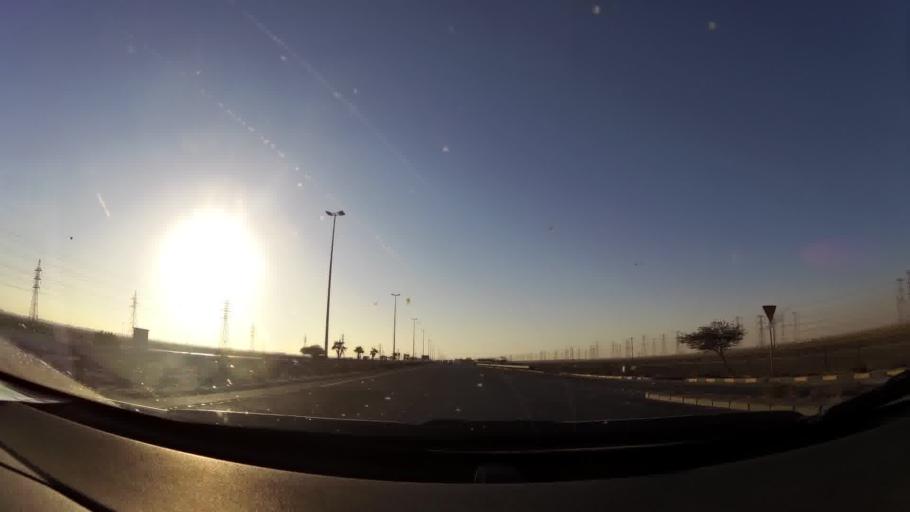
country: KW
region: Al Ahmadi
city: Al Fahahil
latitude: 28.8500
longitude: 48.2446
